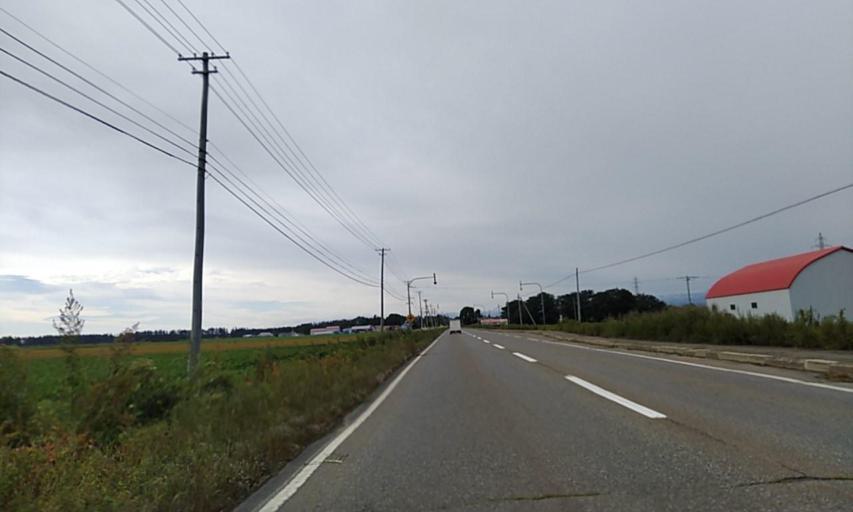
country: JP
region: Hokkaido
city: Obihiro
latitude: 42.7777
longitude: 143.1556
